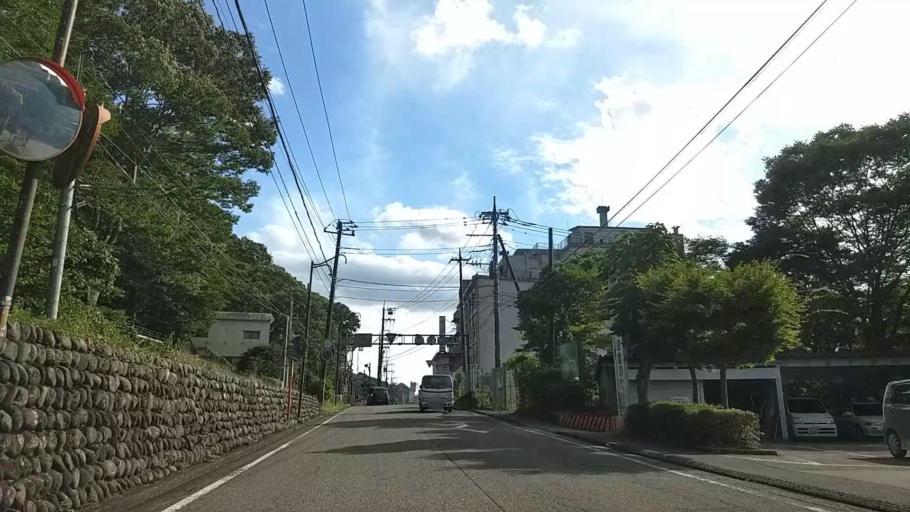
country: JP
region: Tochigi
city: Imaichi
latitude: 36.8316
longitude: 139.7201
